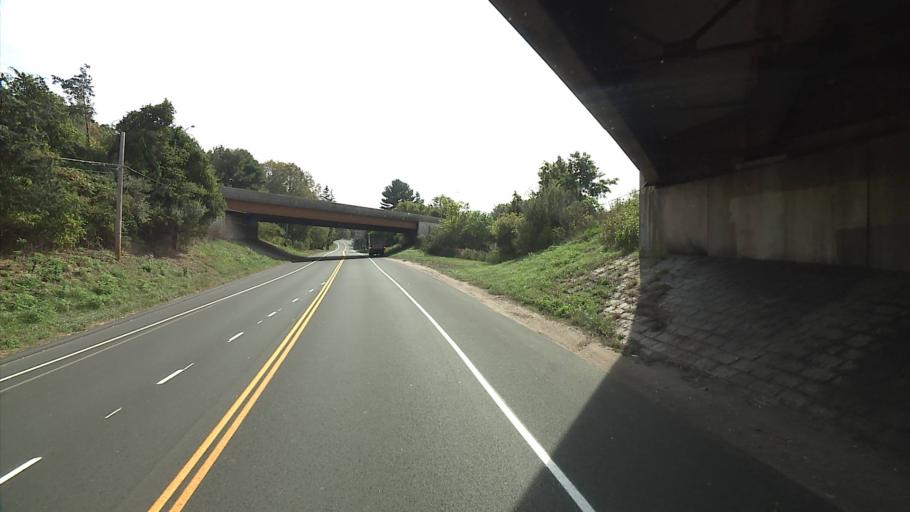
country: US
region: Connecticut
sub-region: Fairfield County
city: Newtown
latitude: 41.4094
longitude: -73.2671
